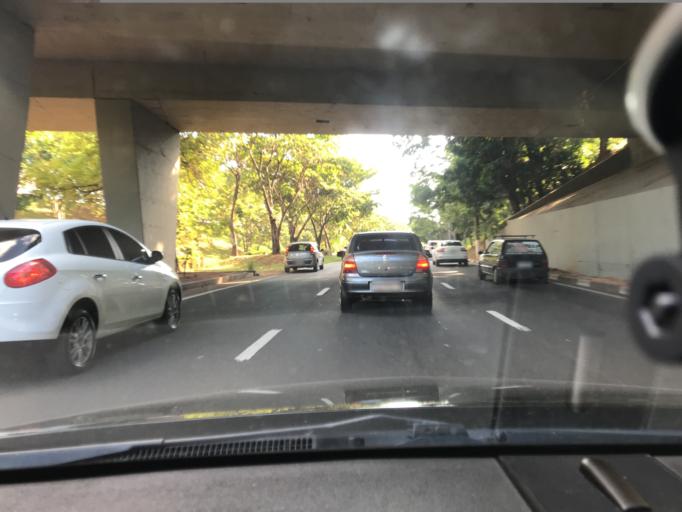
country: BR
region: Sao Paulo
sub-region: Campinas
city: Campinas
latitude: -22.9153
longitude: -47.0596
